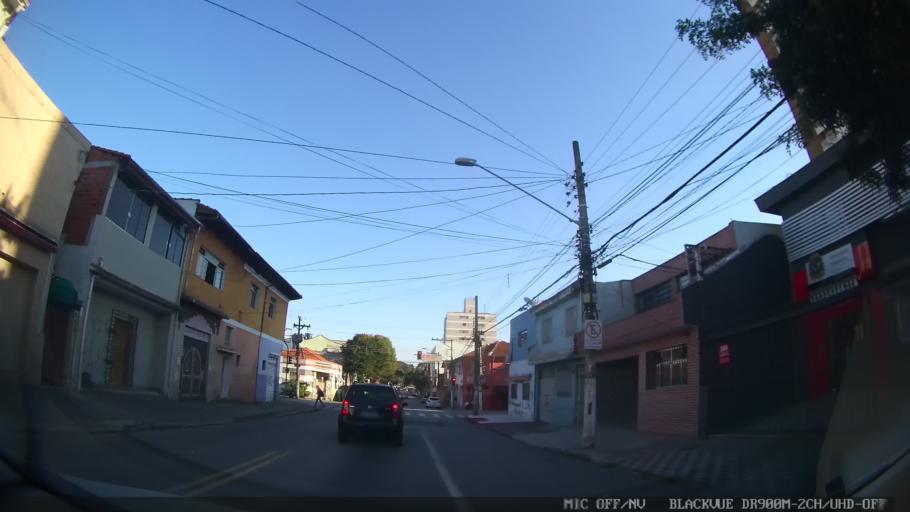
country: BR
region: Sao Paulo
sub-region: Sao Paulo
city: Sao Paulo
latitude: -23.5019
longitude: -46.6212
